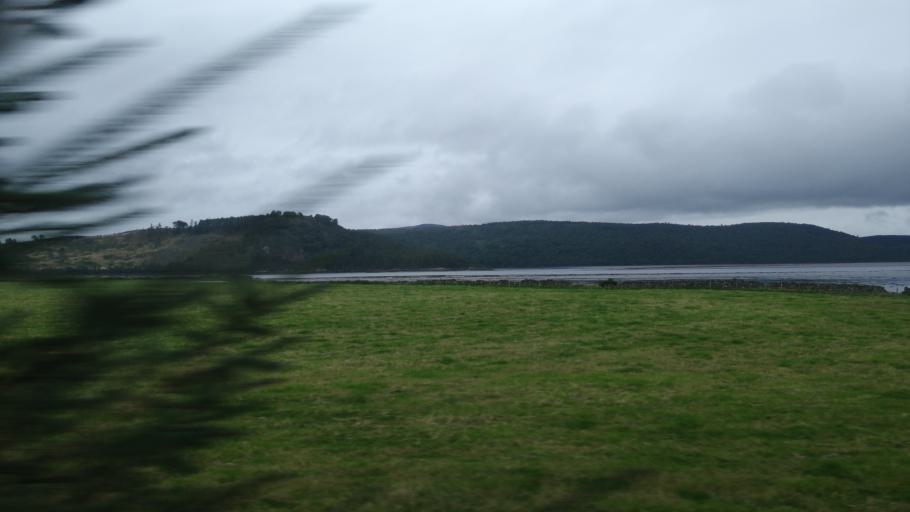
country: GB
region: Scotland
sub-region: Highland
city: Alness
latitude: 57.8505
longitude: -4.2739
